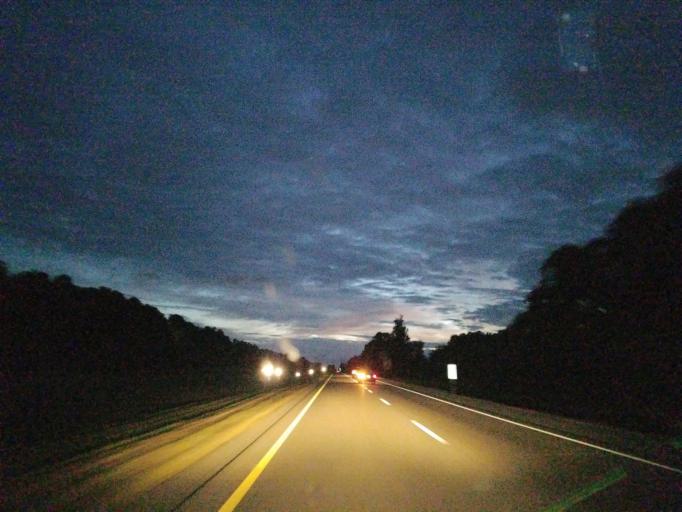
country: US
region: Mississippi
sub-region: Jones County
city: Sharon
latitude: 31.7517
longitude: -89.0739
